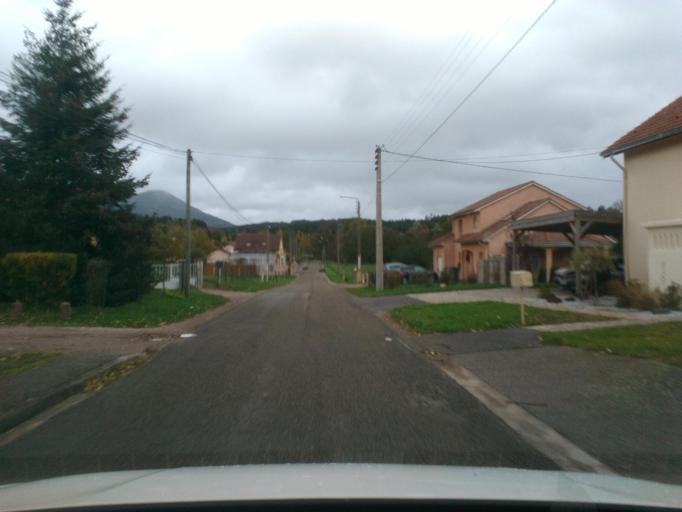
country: FR
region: Lorraine
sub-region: Departement des Vosges
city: Sainte-Marguerite
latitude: 48.2698
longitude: 6.9866
